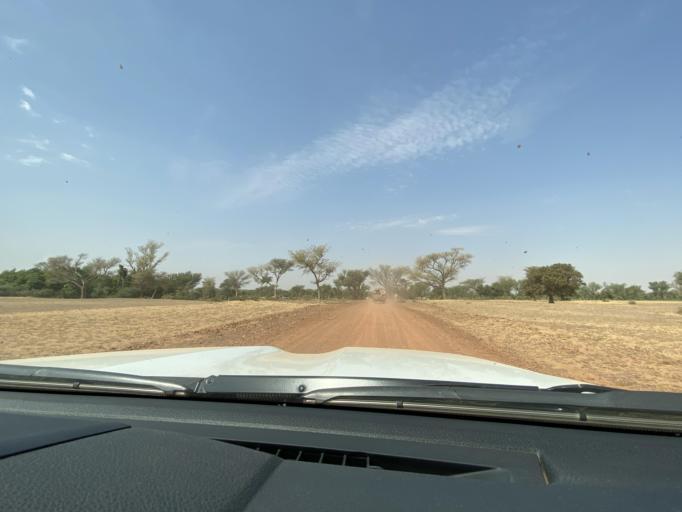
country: NE
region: Dosso
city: Birnin Gaoure
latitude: 13.2458
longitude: 2.8595
